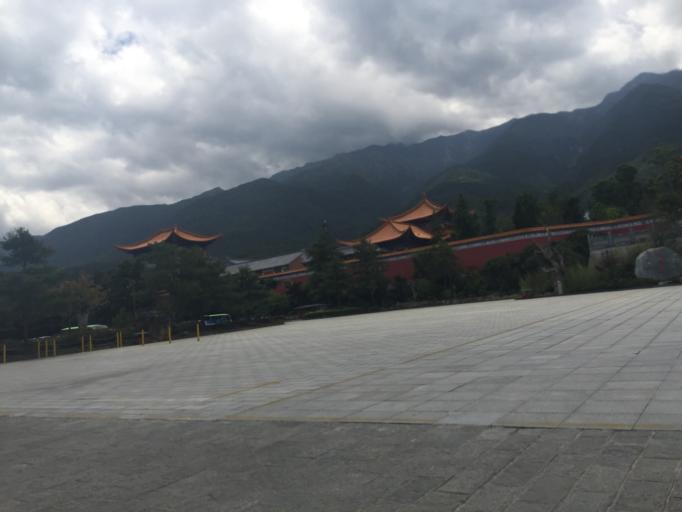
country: CN
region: Yunnan
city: Dali
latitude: 25.7067
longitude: 100.1407
